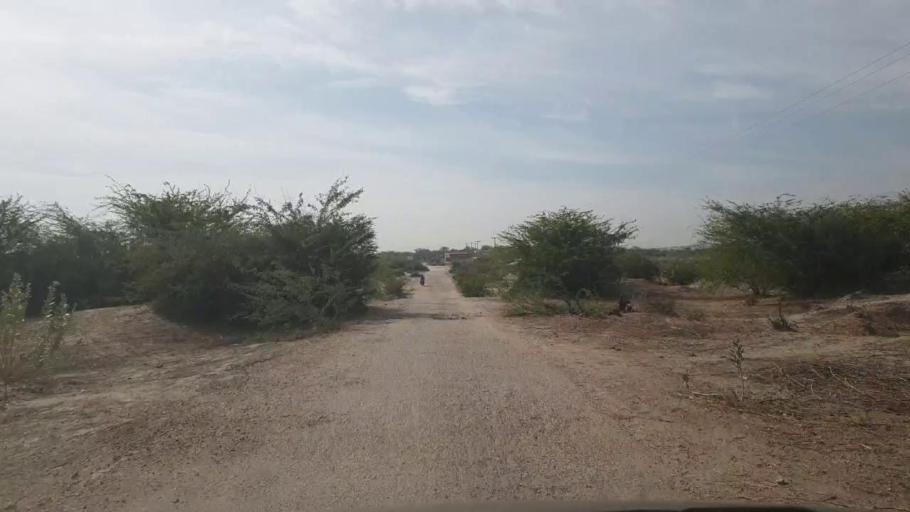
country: PK
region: Sindh
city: Umarkot
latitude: 25.2929
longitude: 69.7380
